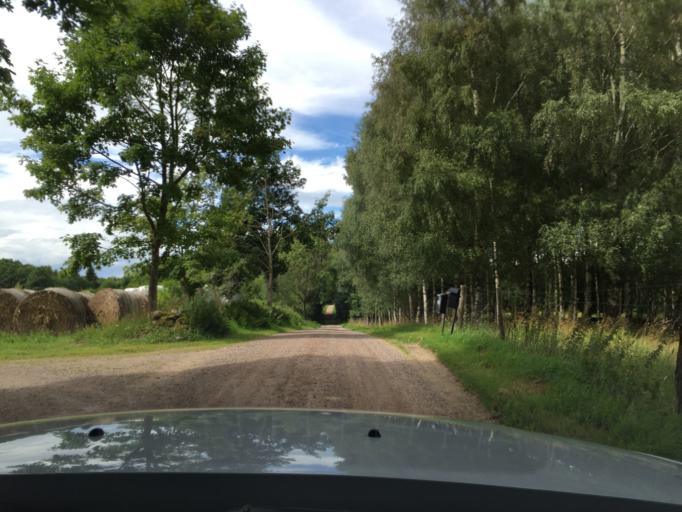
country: SE
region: Skane
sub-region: Hassleholms Kommun
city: Sosdala
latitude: 56.0249
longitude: 13.6446
